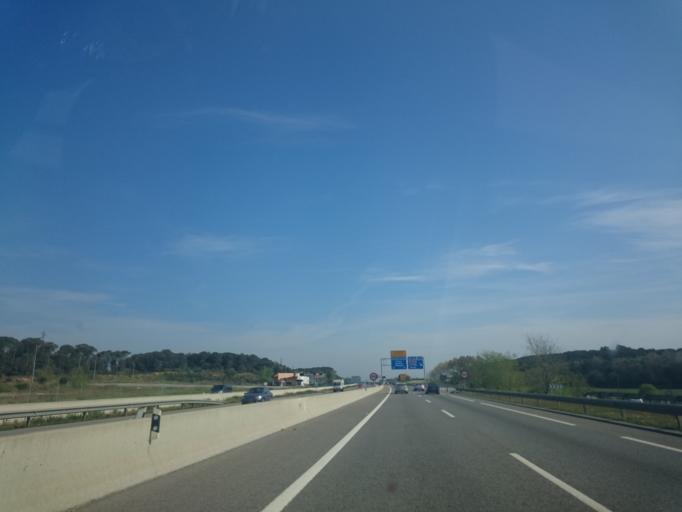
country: ES
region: Catalonia
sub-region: Provincia de Girona
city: Fornells de la Selva
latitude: 41.9146
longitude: 2.7913
